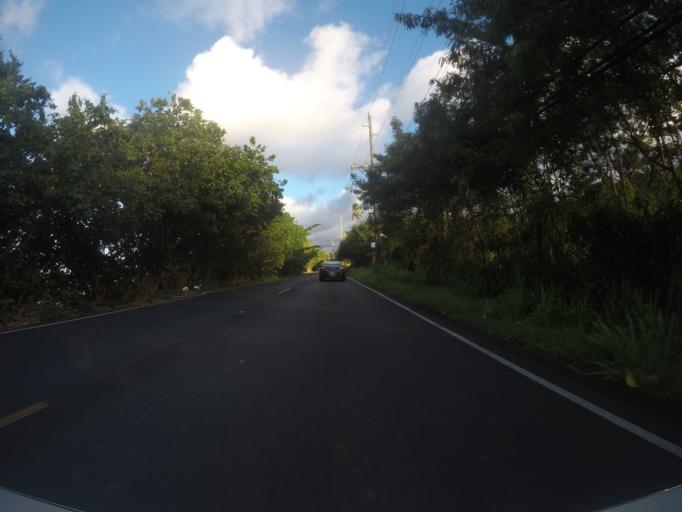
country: US
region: Hawaii
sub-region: Honolulu County
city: He'eia
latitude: 21.4471
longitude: -157.8140
